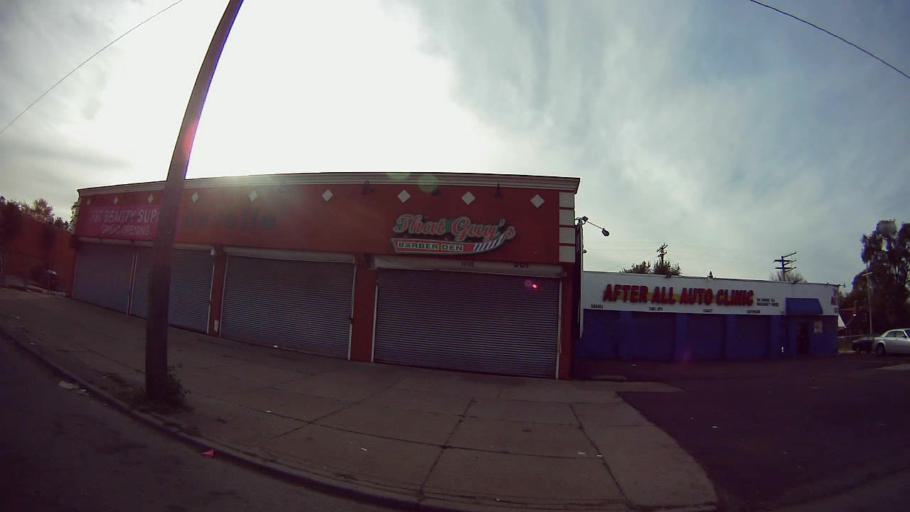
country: US
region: Michigan
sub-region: Oakland County
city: Oak Park
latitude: 42.4166
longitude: -83.1751
